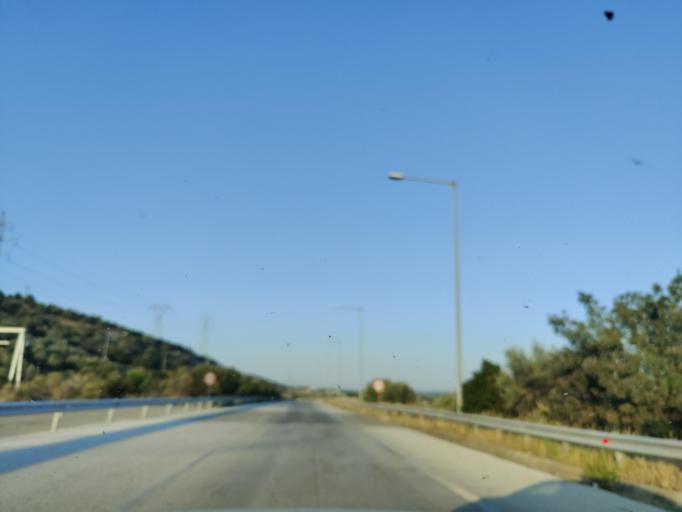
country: GR
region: East Macedonia and Thrace
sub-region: Nomos Kavalas
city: Nea Karvali
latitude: 40.9677
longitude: 24.5308
